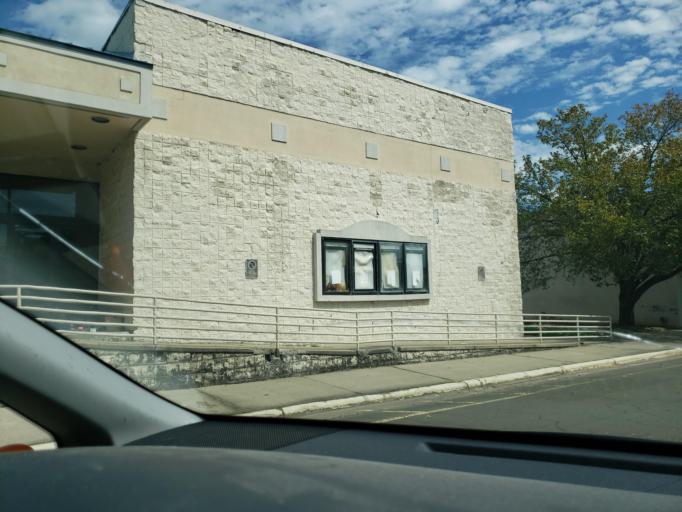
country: US
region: North Carolina
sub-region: Durham County
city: Durham
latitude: 36.0188
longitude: -78.8868
